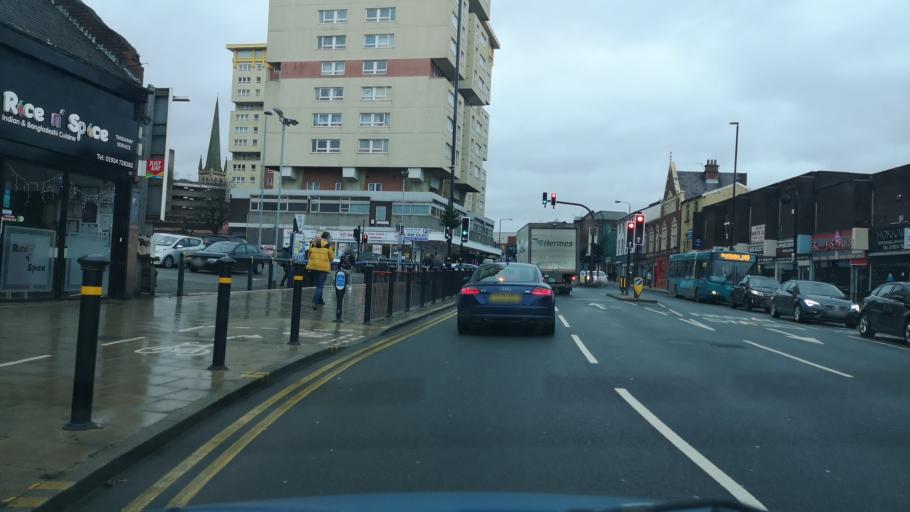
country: GB
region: England
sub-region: City and Borough of Wakefield
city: Wakefield
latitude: 53.6808
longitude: -1.4927
